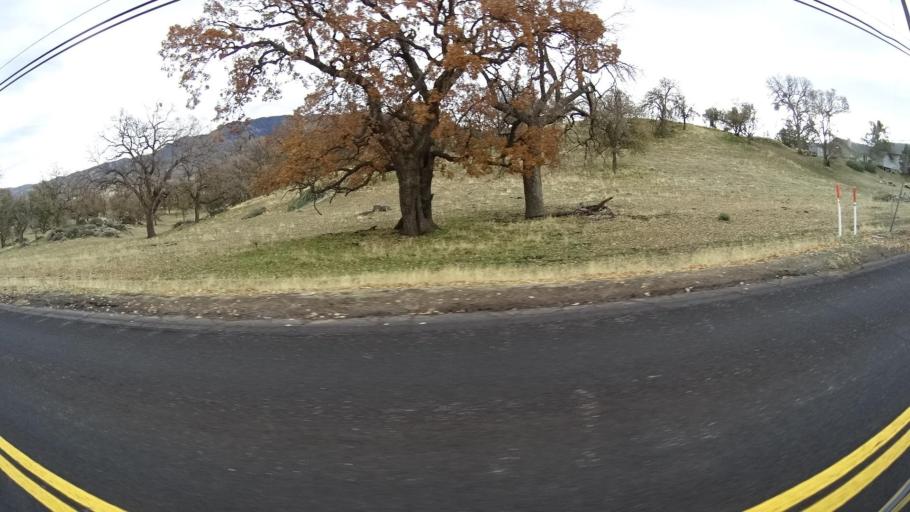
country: US
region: California
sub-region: Kern County
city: Stallion Springs
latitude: 35.0933
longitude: -118.6487
